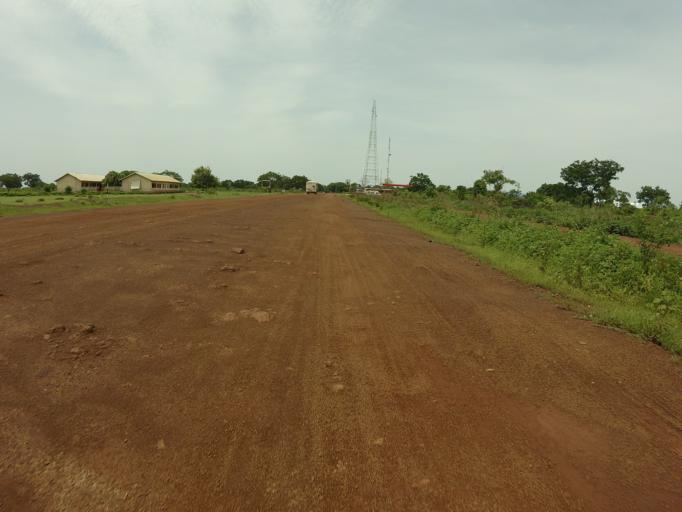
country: GH
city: Kpandae
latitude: 8.8746
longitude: 0.0415
